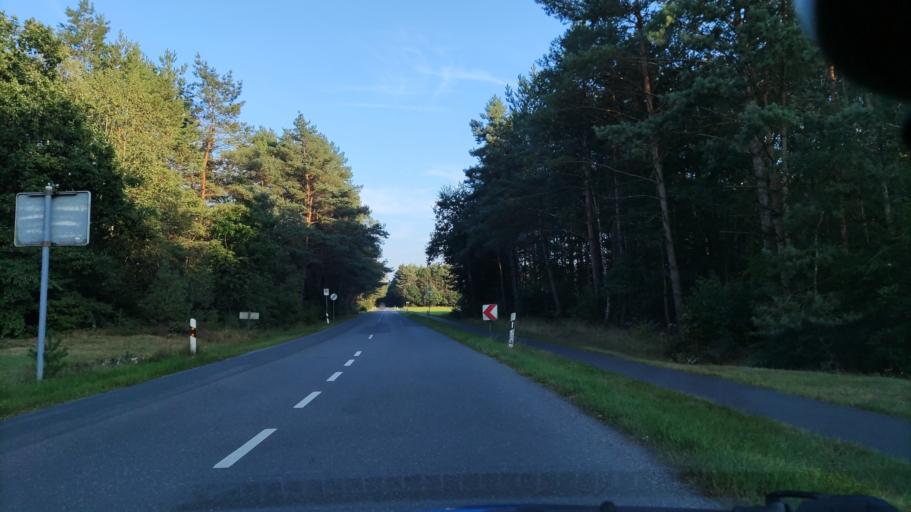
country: DE
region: Lower Saxony
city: Munster
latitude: 52.9735
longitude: 10.1467
